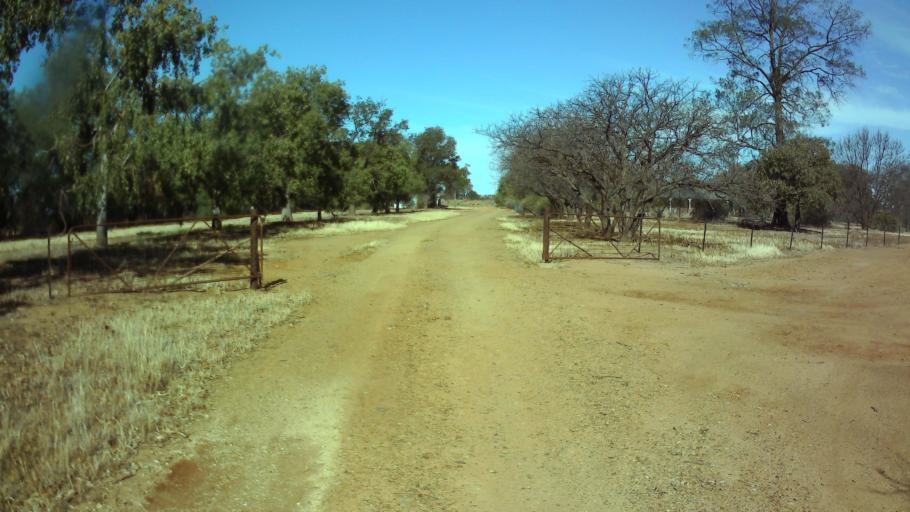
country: AU
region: New South Wales
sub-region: Weddin
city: Grenfell
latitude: -33.7336
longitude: 148.0943
